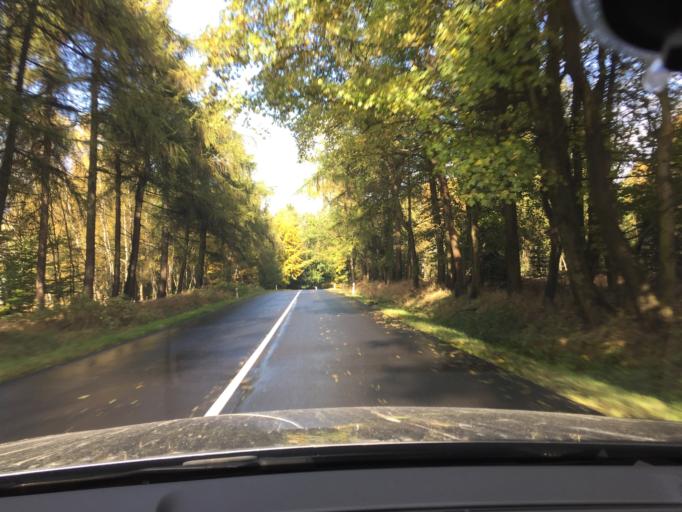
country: CZ
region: Ustecky
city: Libouchec
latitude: 50.7626
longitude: 13.9727
